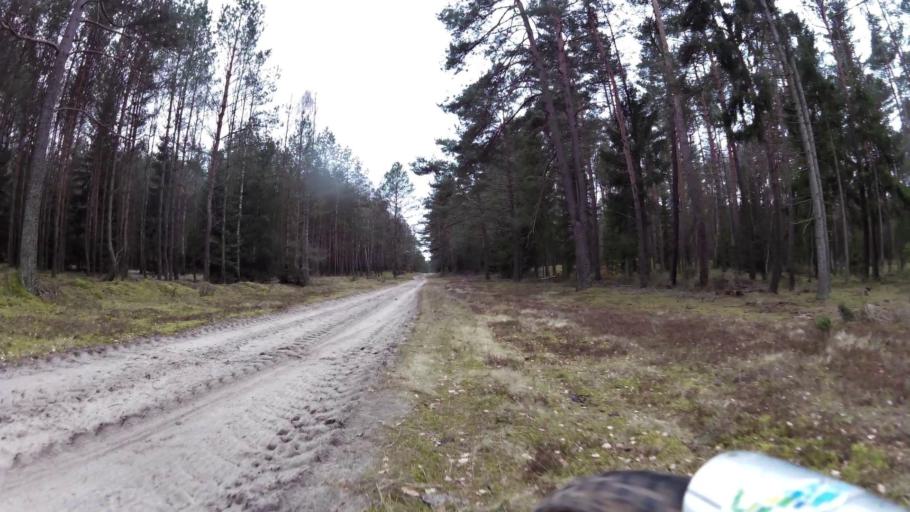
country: PL
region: Pomeranian Voivodeship
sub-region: Powiat bytowski
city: Trzebielino
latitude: 54.1259
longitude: 17.1331
